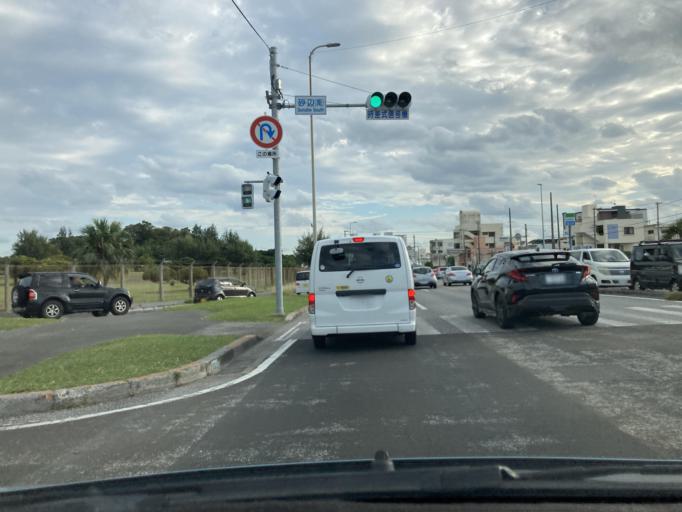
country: JP
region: Okinawa
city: Chatan
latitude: 26.3317
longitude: 127.7518
